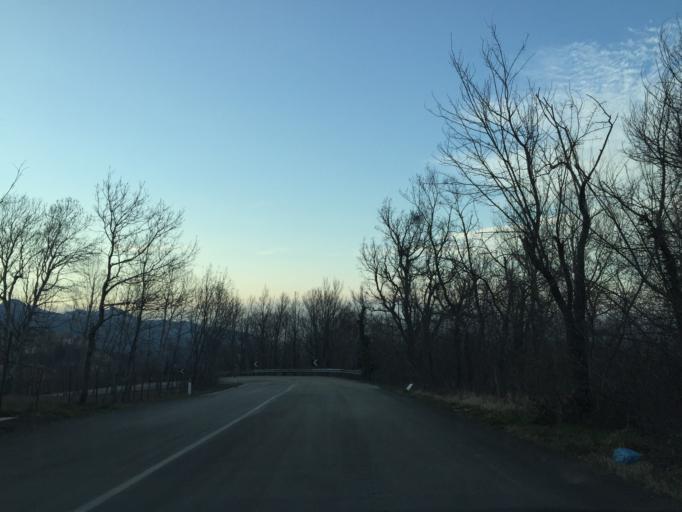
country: IT
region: Molise
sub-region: Provincia di Campobasso
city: Guardiaregia
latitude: 41.4347
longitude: 14.5469
